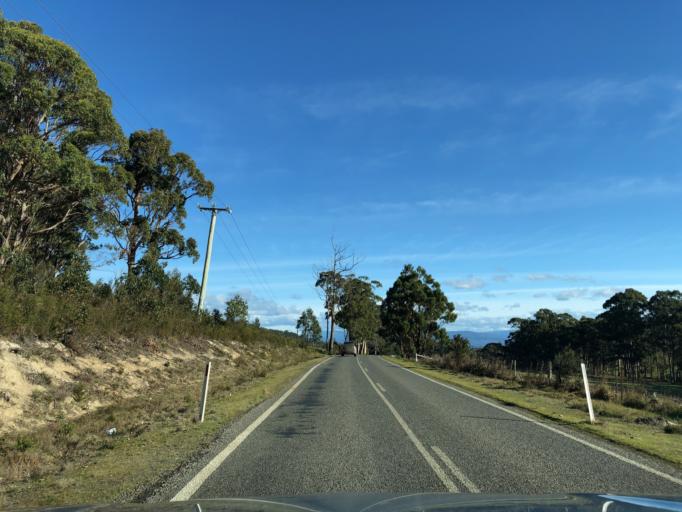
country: AU
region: Tasmania
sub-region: Kingborough
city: Kettering
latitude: -43.3144
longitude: 147.2723
